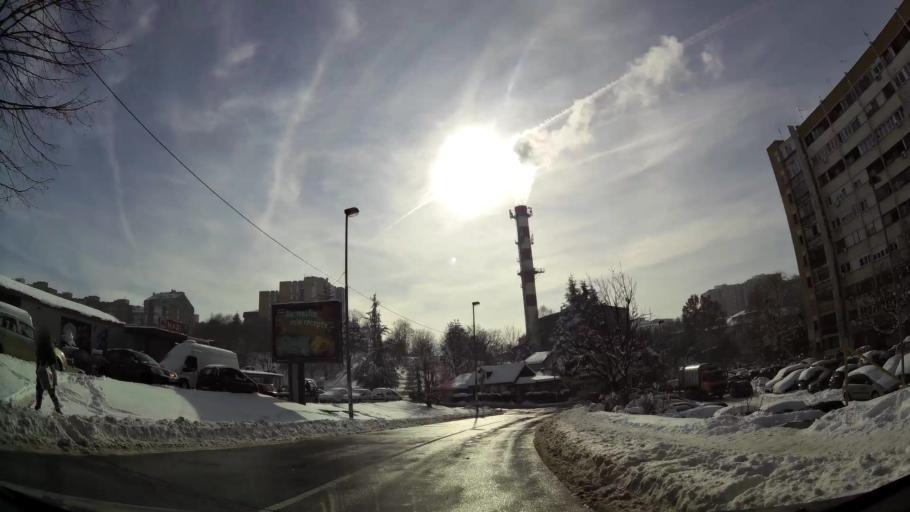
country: RS
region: Central Serbia
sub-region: Belgrade
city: Zvezdara
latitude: 44.7902
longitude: 20.5339
